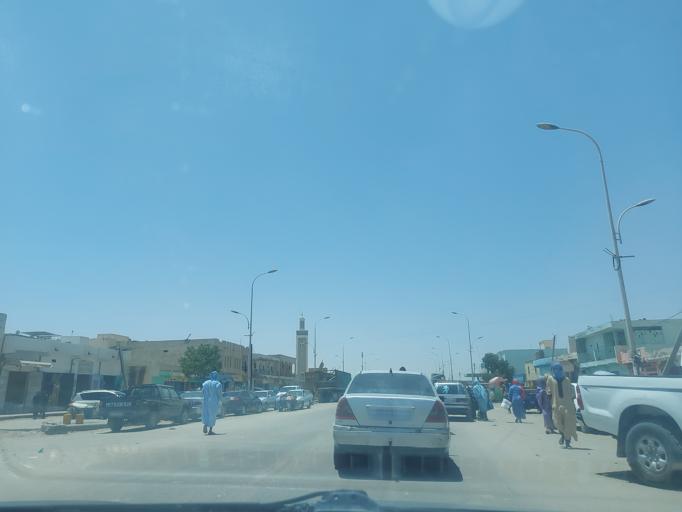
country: MR
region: Nouakchott
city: Nouakchott
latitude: 18.0802
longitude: -15.9818
